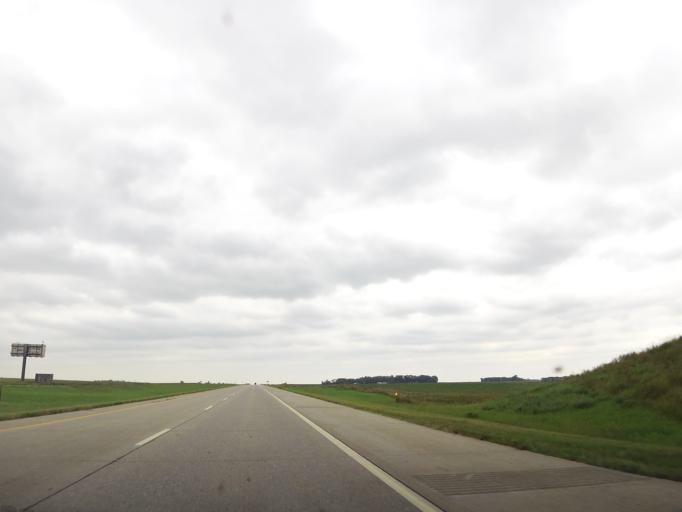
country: US
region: South Dakota
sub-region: Roberts County
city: Sisseton
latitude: 45.6888
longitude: -96.9702
